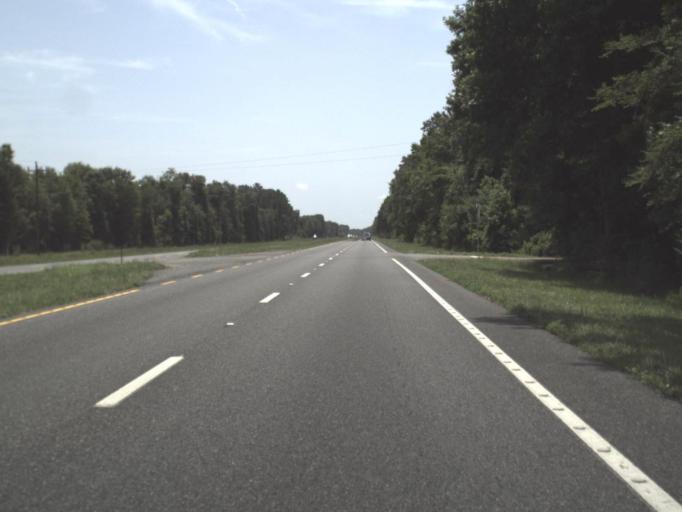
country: US
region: Florida
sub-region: Taylor County
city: Steinhatchee
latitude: 29.8993
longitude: -83.4220
